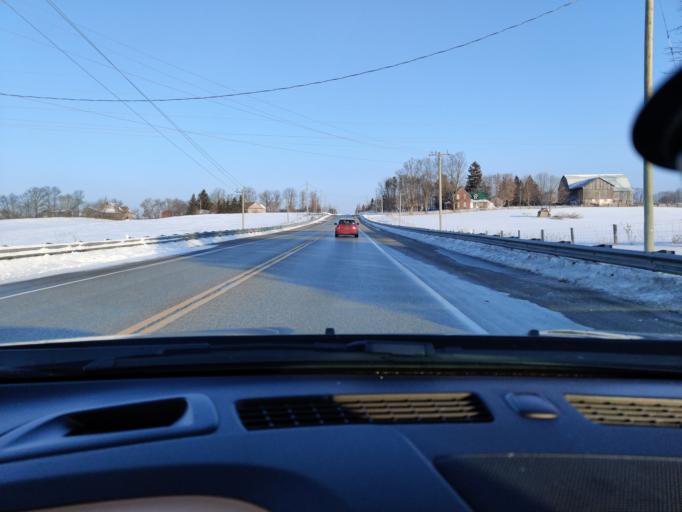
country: CA
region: Ontario
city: Angus
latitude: 44.3766
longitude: -79.7836
